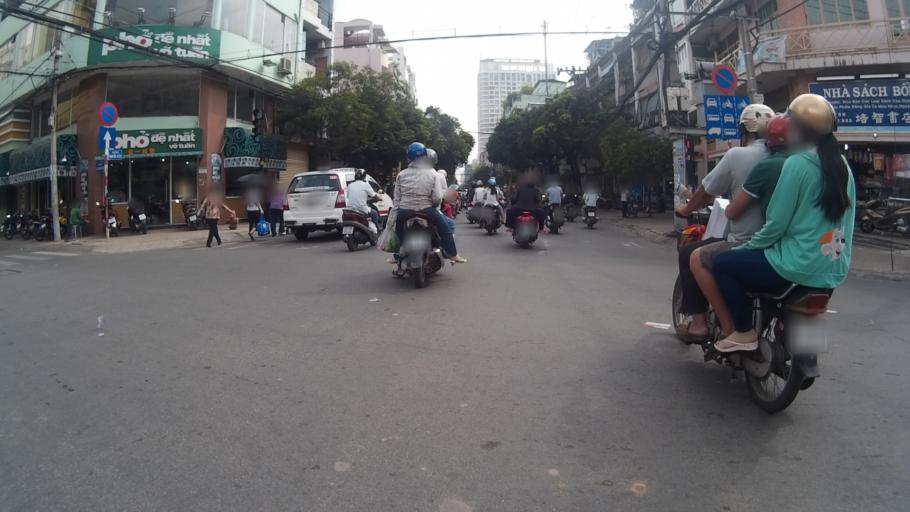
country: VN
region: Ho Chi Minh City
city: Quan Nam
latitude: 10.7530
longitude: 106.6613
